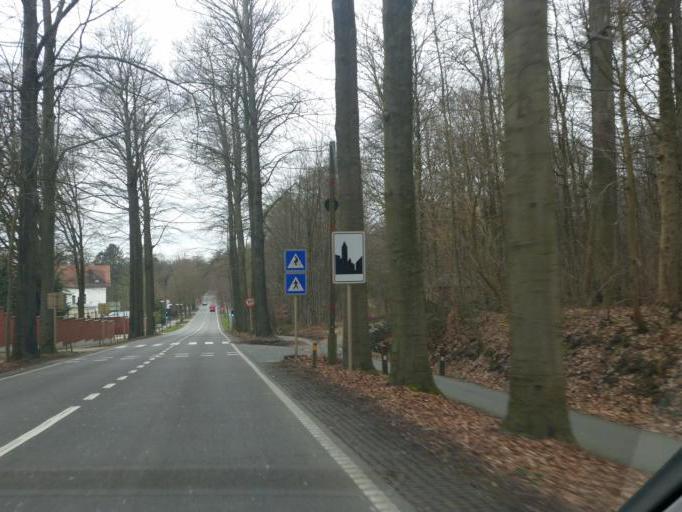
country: BE
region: Flanders
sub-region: Provincie Vlaams-Brabant
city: Sint-Genesius-Rode
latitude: 50.7832
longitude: 4.3875
